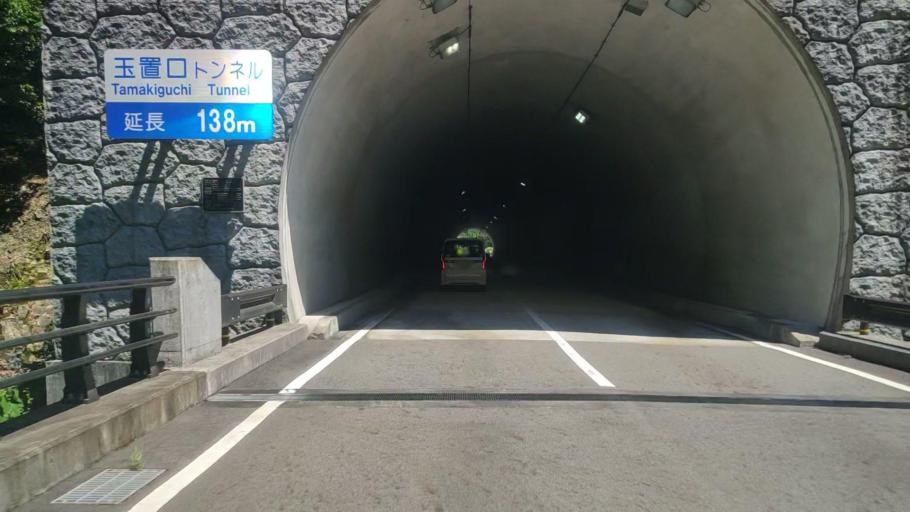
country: JP
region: Wakayama
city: Shingu
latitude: 33.8896
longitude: 135.8798
